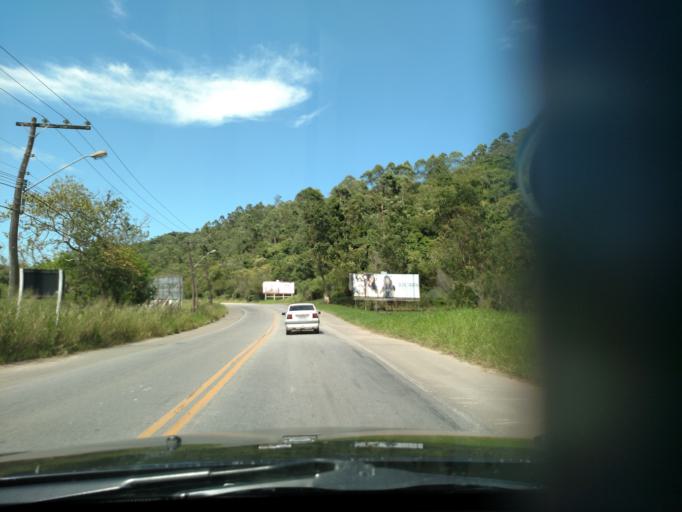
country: BR
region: Santa Catarina
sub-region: Itajai
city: Itajai
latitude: -26.8916
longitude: -48.7608
